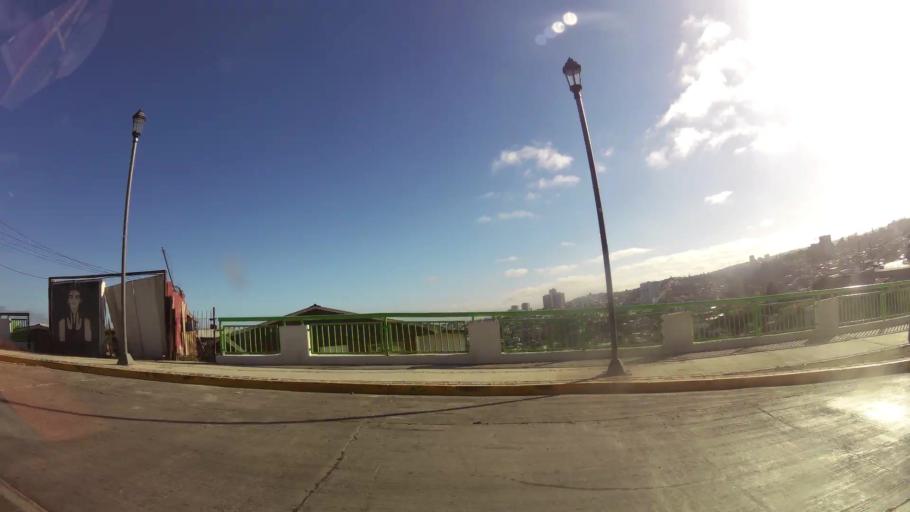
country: CL
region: Valparaiso
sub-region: Provincia de Valparaiso
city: Valparaiso
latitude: -33.0555
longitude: -71.6093
